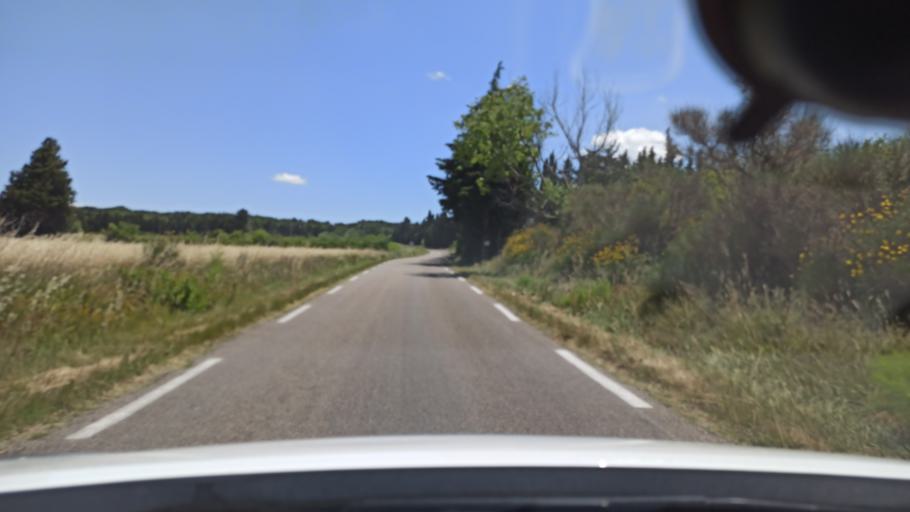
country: FR
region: Provence-Alpes-Cote d'Azur
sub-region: Departement du Vaucluse
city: Chateauneuf-de-Gadagne
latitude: 43.9092
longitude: 4.9184
